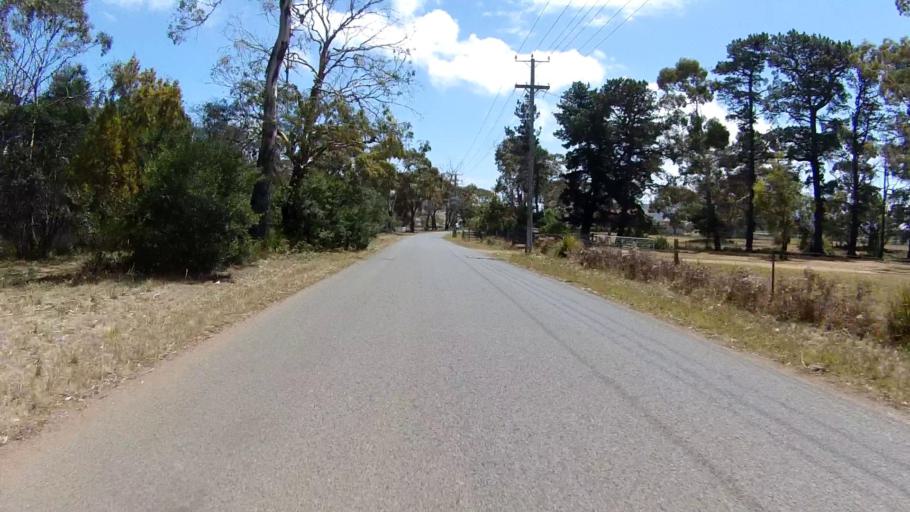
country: AU
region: Tasmania
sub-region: Clarence
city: Sandford
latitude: -42.9293
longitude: 147.4947
